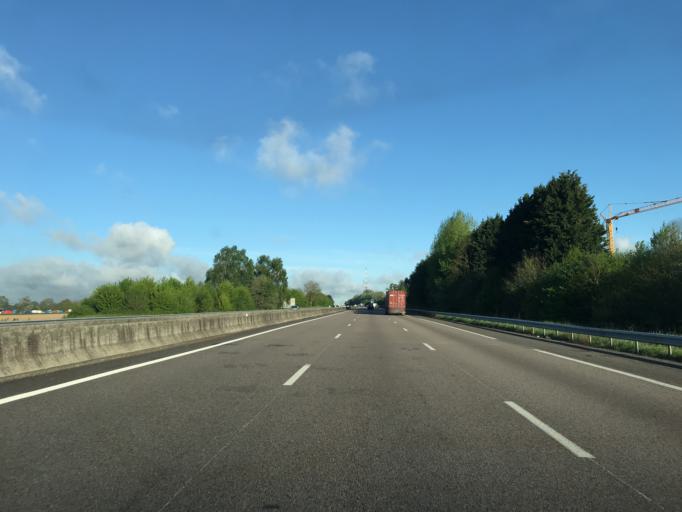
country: FR
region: Haute-Normandie
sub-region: Departement de l'Eure
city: Saint-Ouen-de-Thouberville
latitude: 49.3552
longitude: 0.8810
